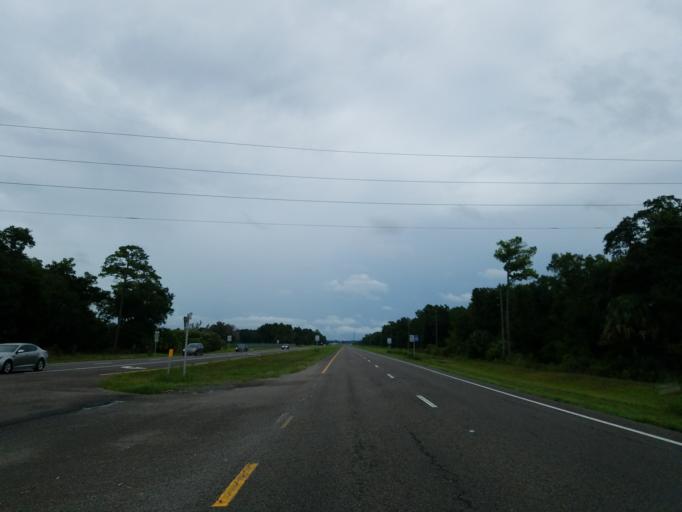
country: US
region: Florida
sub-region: Sumter County
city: Wildwood
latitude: 28.8795
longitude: -82.1201
